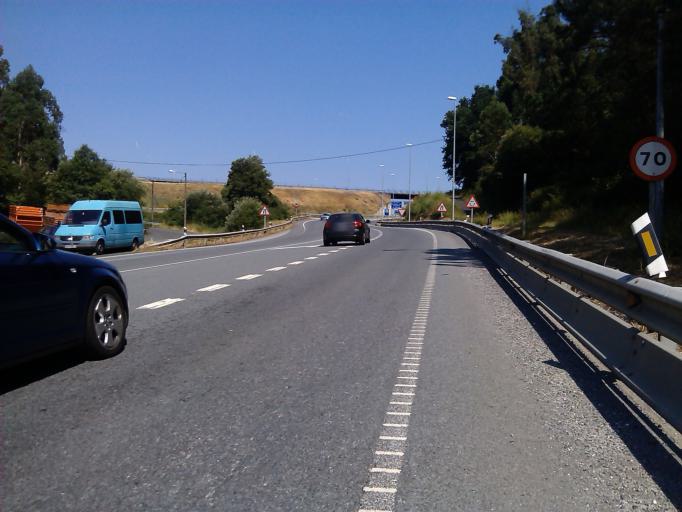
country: ES
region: Galicia
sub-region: Provincia da Coruna
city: Santiago de Compostela
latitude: 42.8533
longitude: -8.5286
